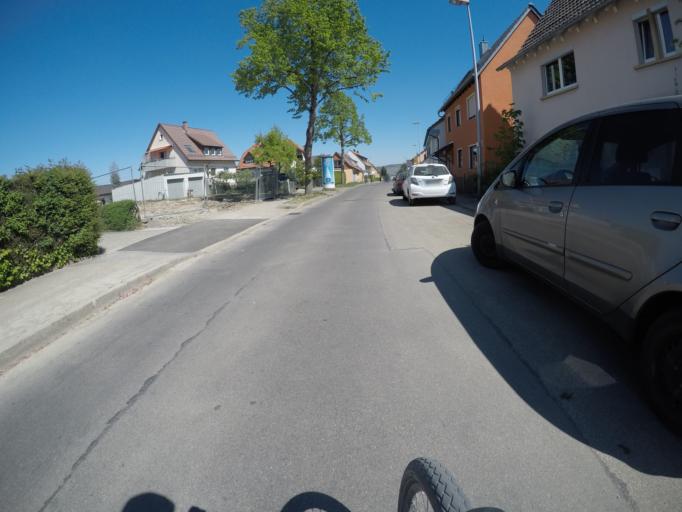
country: DE
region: Baden-Wuerttemberg
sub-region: Regierungsbezirk Stuttgart
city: Waiblingen
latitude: 48.8032
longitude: 9.3190
